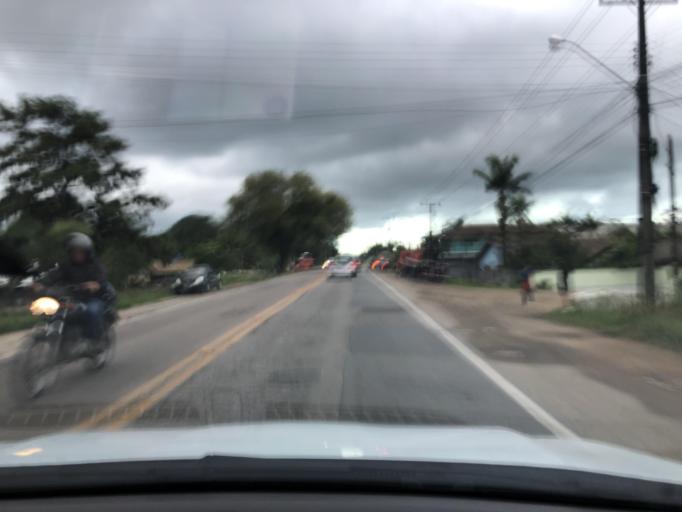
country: BR
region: Santa Catarina
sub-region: Sao Francisco Do Sul
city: Sao Francisco do Sul
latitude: -26.2492
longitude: -48.6075
